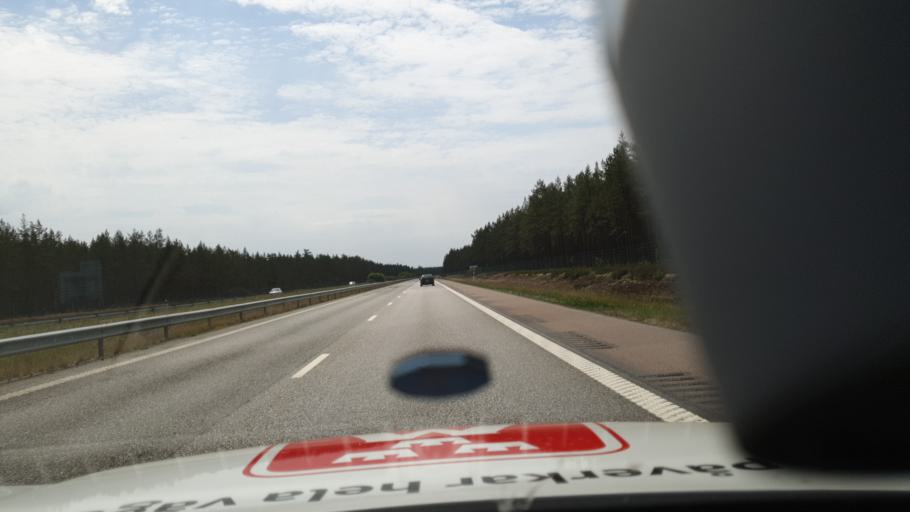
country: SE
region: Joenkoeping
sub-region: Vaggeryds Kommun
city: Skillingaryd
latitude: 57.3326
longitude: 14.1003
